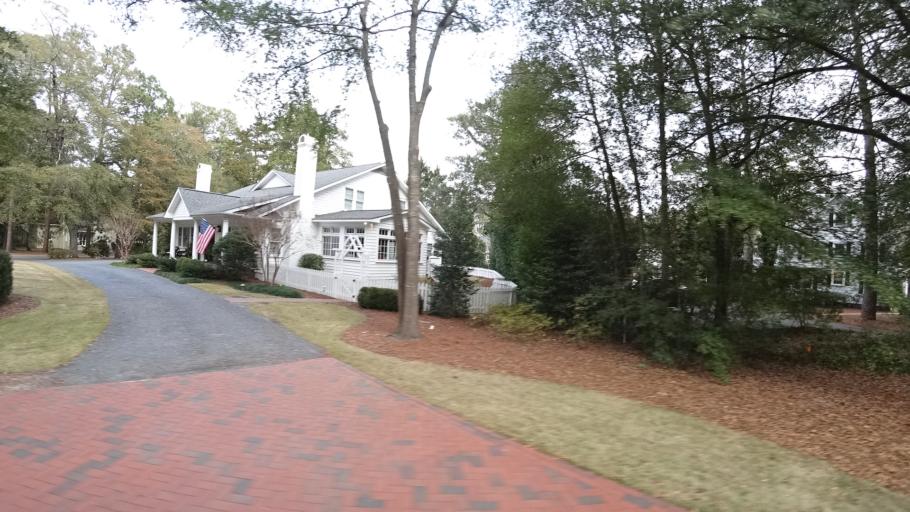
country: US
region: North Carolina
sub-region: Moore County
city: Pinehurst
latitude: 35.1966
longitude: -79.4654
